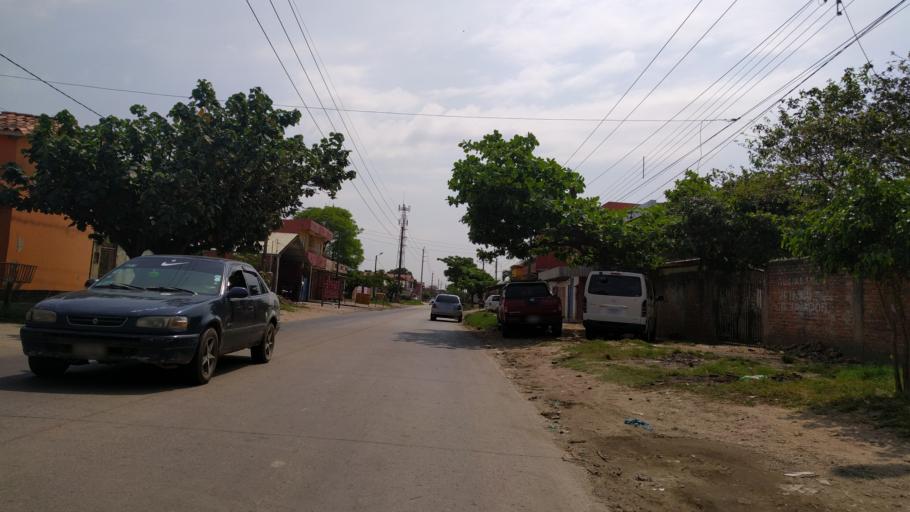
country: BO
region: Santa Cruz
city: Santa Cruz de la Sierra
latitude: -17.8347
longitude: -63.2131
